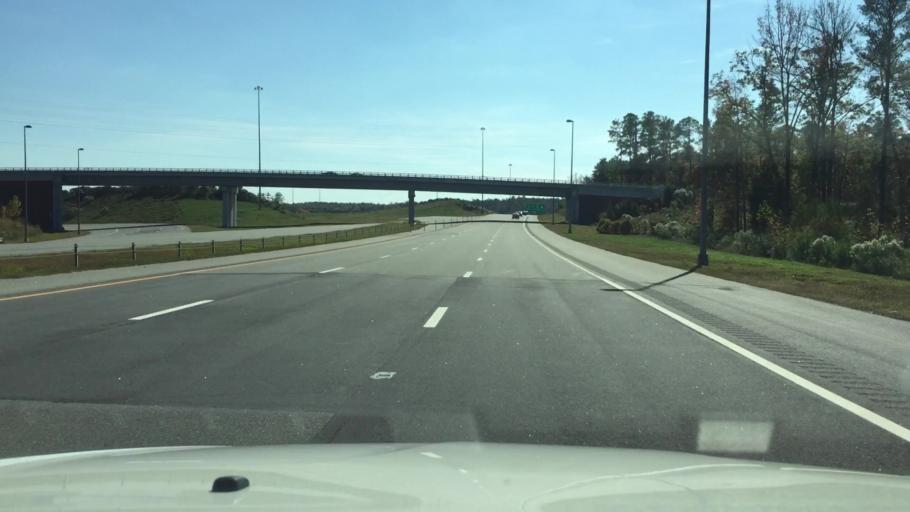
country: US
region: North Carolina
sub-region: Wake County
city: Morrisville
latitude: 35.8603
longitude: -78.8640
